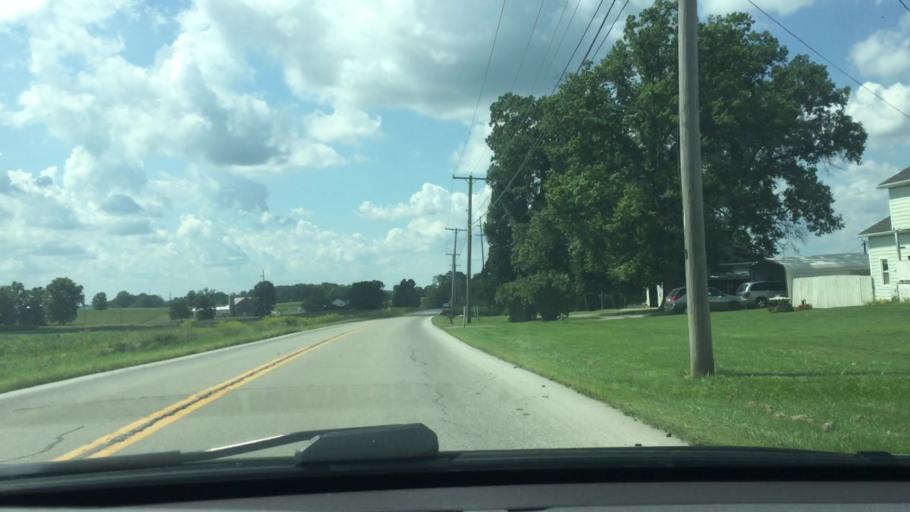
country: US
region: Pennsylvania
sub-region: Lawrence County
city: New Wilmington
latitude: 41.1201
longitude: -80.3829
